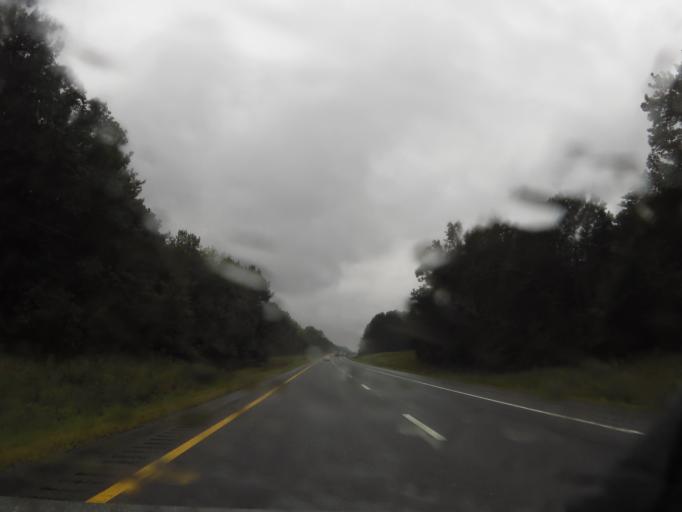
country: US
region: Tennessee
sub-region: Bradley County
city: Hopewell
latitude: 35.2531
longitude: -84.8386
